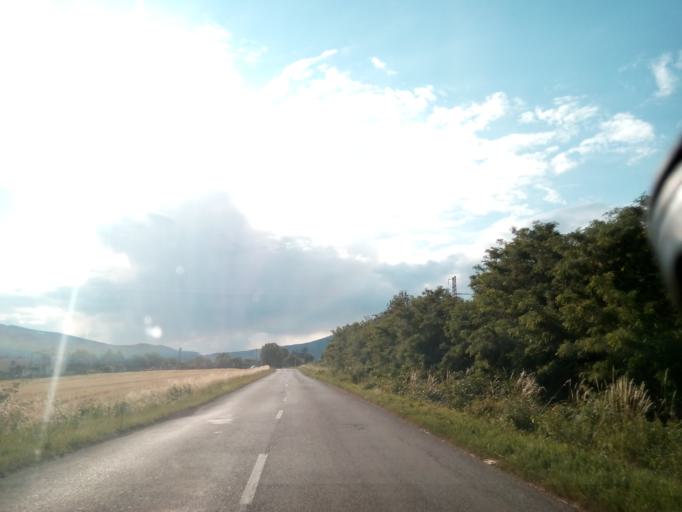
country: SK
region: Kosicky
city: Secovce
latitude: 48.6142
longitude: 21.5383
